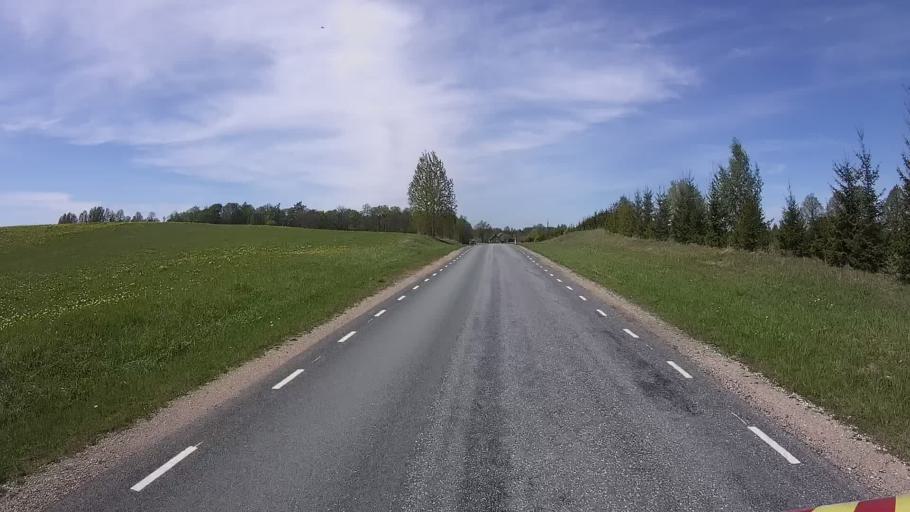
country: EE
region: Valgamaa
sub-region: Valga linn
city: Valga
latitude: 57.6503
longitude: 26.3061
